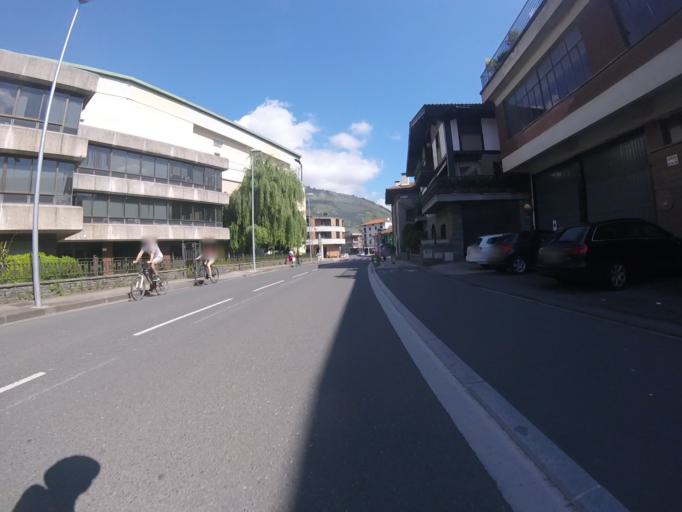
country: ES
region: Basque Country
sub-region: Provincia de Guipuzcoa
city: Azpeitia
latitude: 43.1768
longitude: -2.2585
